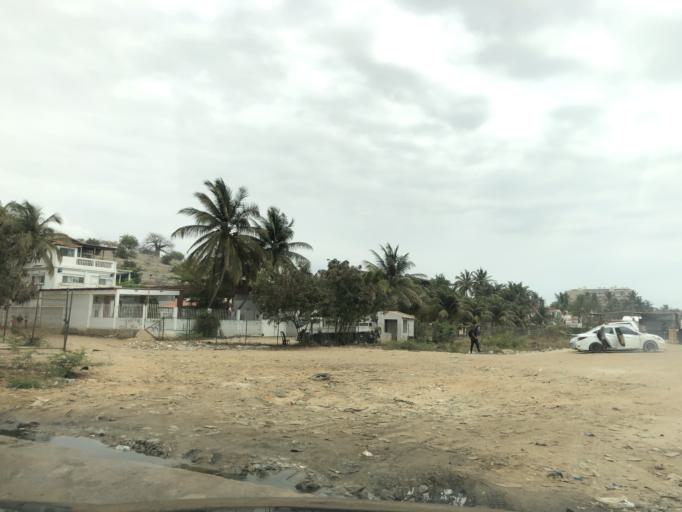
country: AO
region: Luanda
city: Luanda
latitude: -8.8729
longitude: 13.1929
